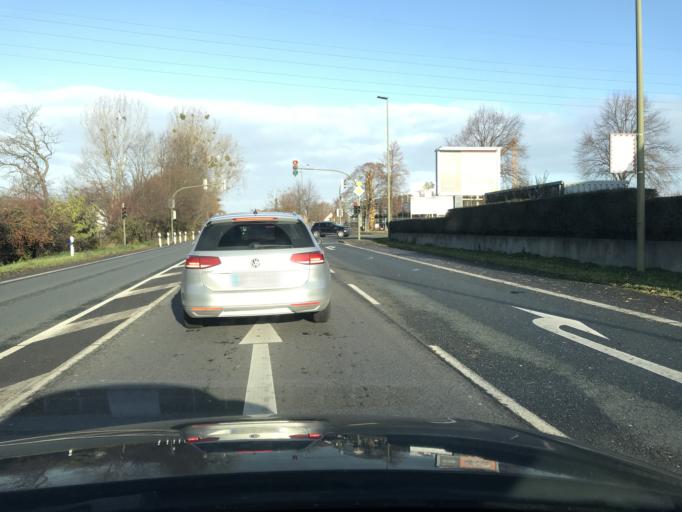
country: DE
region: North Rhine-Westphalia
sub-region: Regierungsbezirk Arnsberg
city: Hamm
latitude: 51.6432
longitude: 7.8440
